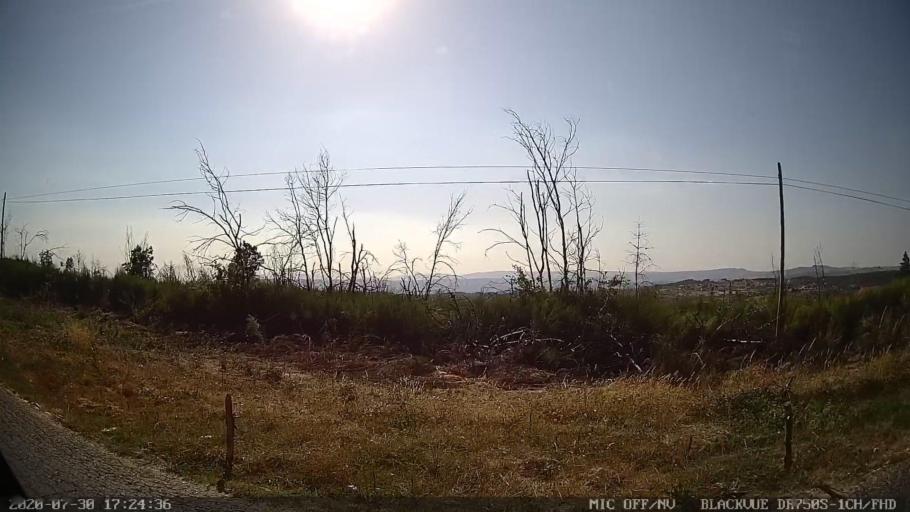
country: PT
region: Vila Real
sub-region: Murca
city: Murca
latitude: 41.3127
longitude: -7.4705
